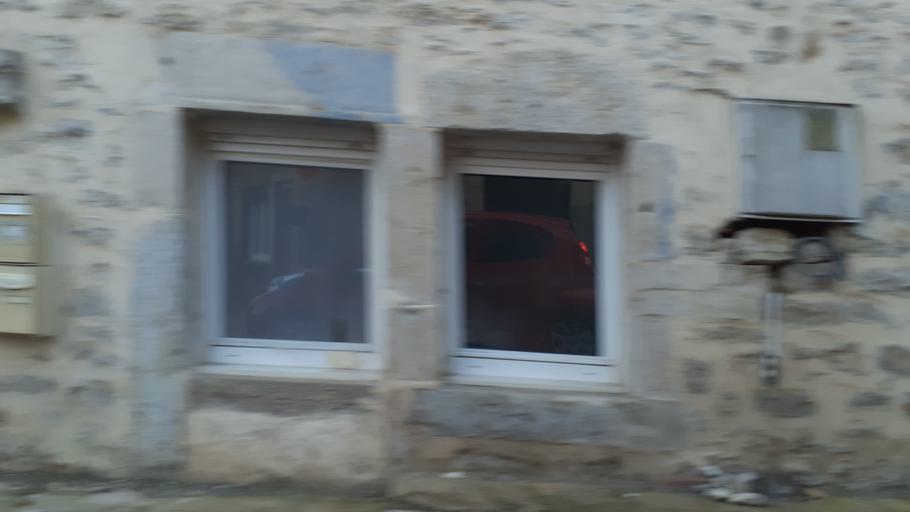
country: FR
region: Franche-Comte
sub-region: Departement du Doubs
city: Novillars
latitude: 47.2830
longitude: 6.1523
